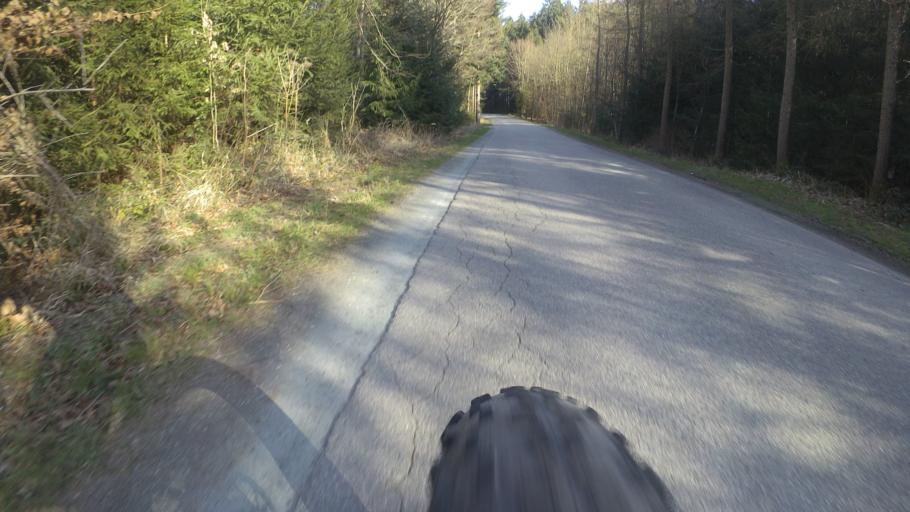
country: DE
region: Bavaria
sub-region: Upper Bavaria
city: Traunreut
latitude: 47.9416
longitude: 12.5765
